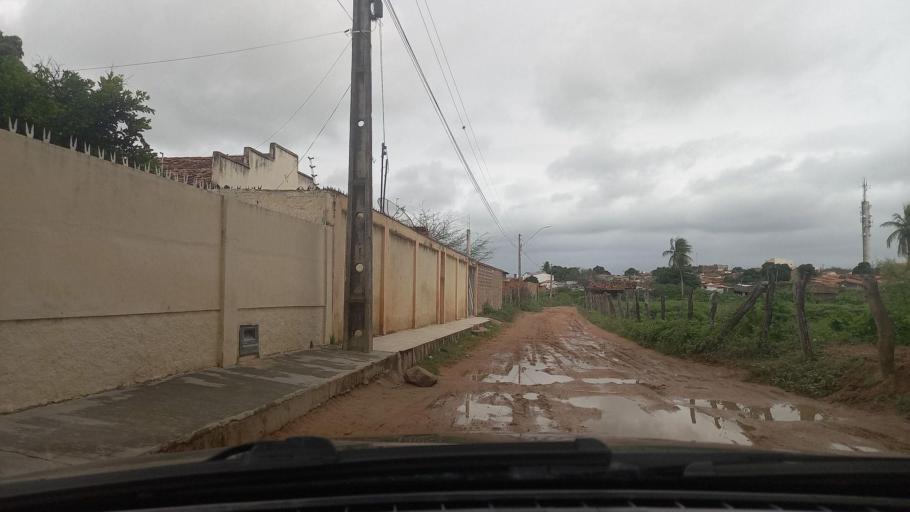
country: BR
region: Alagoas
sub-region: Delmiro Gouveia
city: Delmiro Gouveia
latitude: -9.3884
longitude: -37.9938
